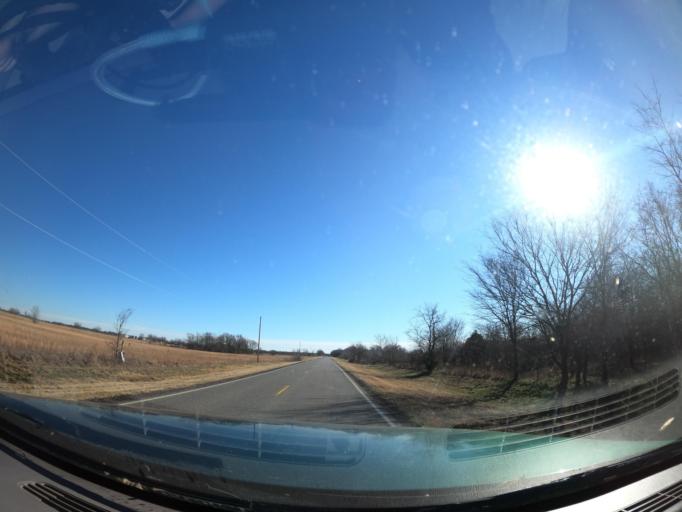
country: US
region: Oklahoma
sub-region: McIntosh County
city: Checotah
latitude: 35.5708
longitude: -95.6570
